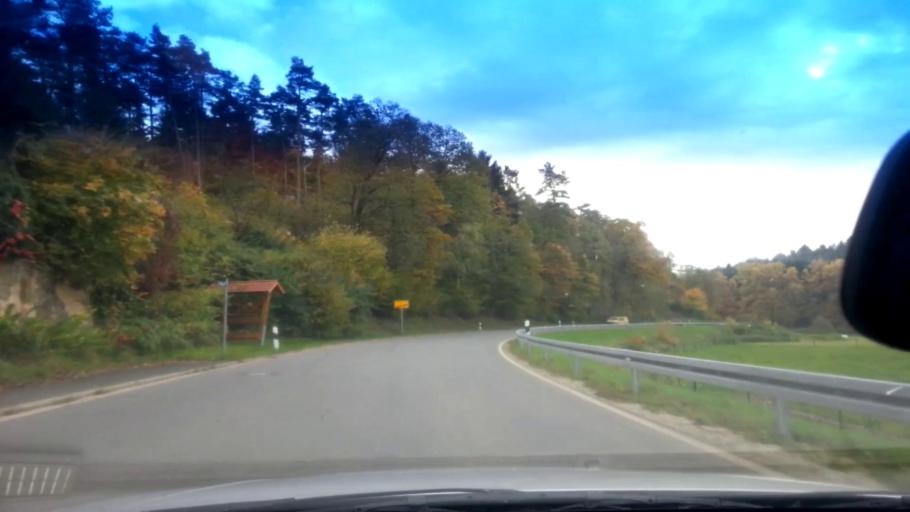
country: DE
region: Bavaria
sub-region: Upper Franconia
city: Wonsees
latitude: 49.9996
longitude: 11.3002
